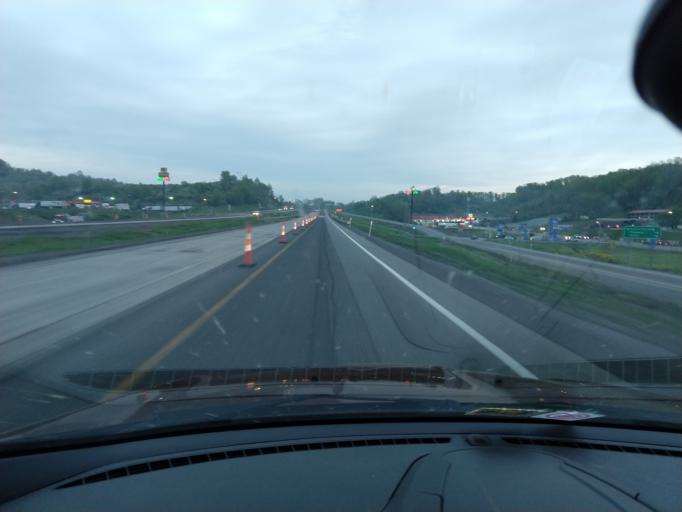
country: US
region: West Virginia
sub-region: Braxton County
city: Sutton
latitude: 38.7015
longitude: -80.6643
